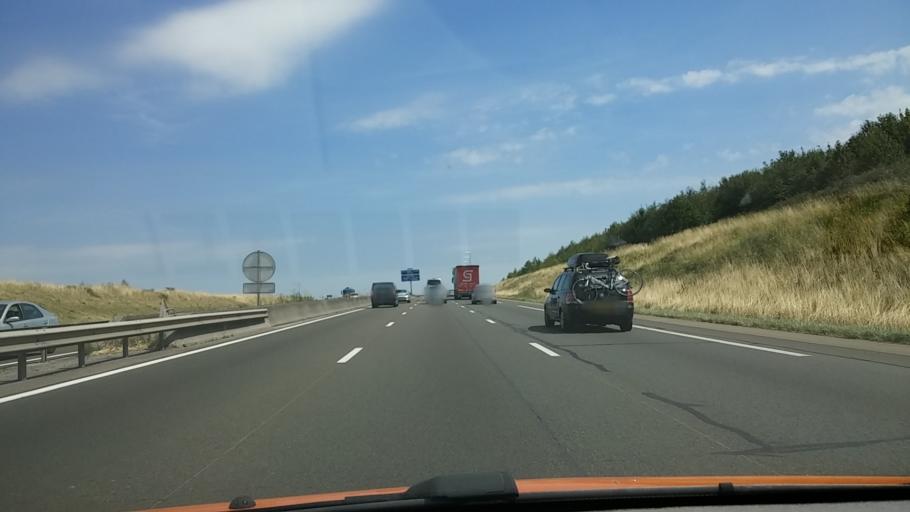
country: FR
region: Ile-de-France
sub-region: Departement de Seine-et-Marne
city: Bussy-Saint-Georges
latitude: 48.8305
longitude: 2.6960
